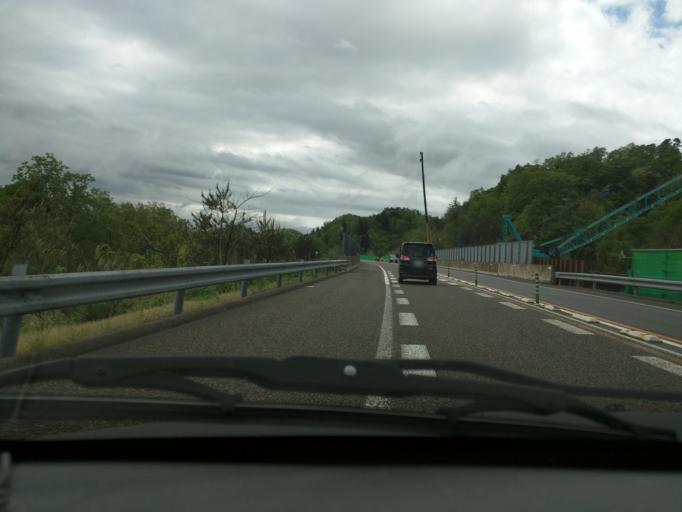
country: JP
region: Niigata
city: Joetsu
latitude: 37.1226
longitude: 138.2133
